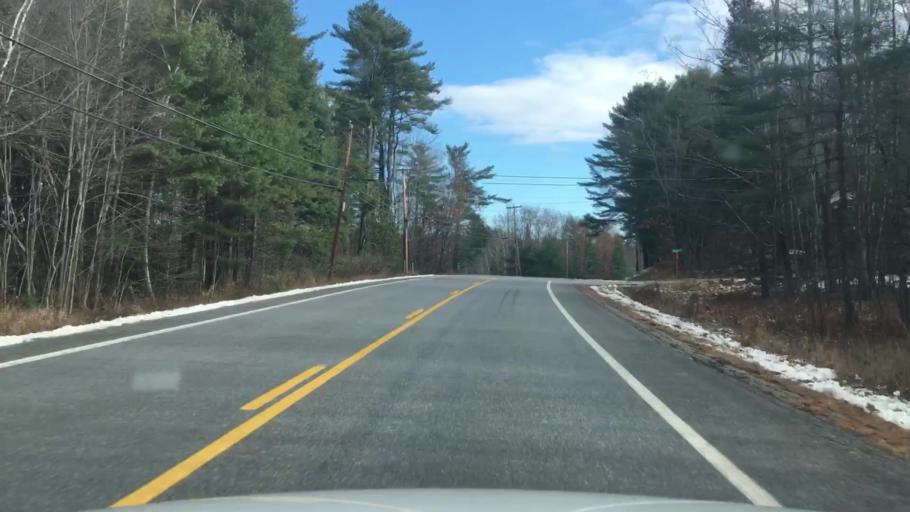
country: US
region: Maine
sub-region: Kennebec County
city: Wayne
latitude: 44.3493
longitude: -70.0519
